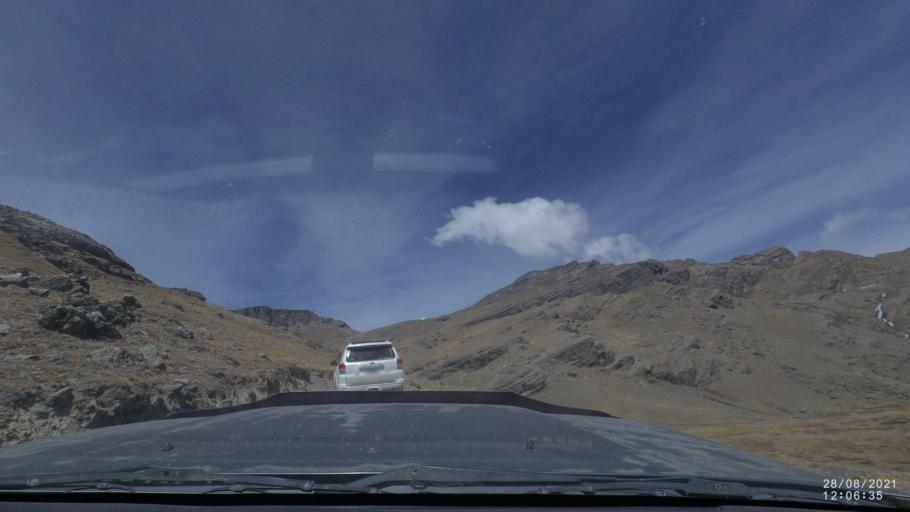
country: BO
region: Cochabamba
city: Sipe Sipe
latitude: -17.2712
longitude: -66.3827
